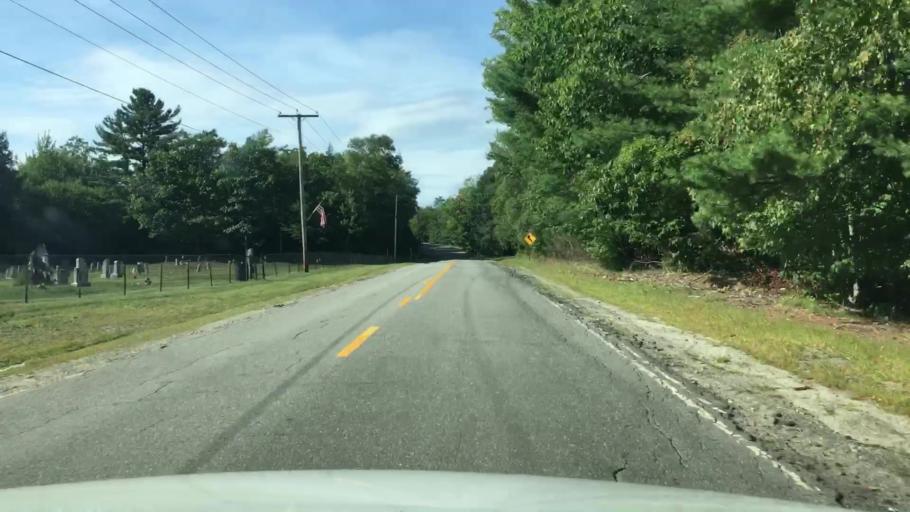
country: US
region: Maine
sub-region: Penobscot County
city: Enfield
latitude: 45.2223
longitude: -68.5375
